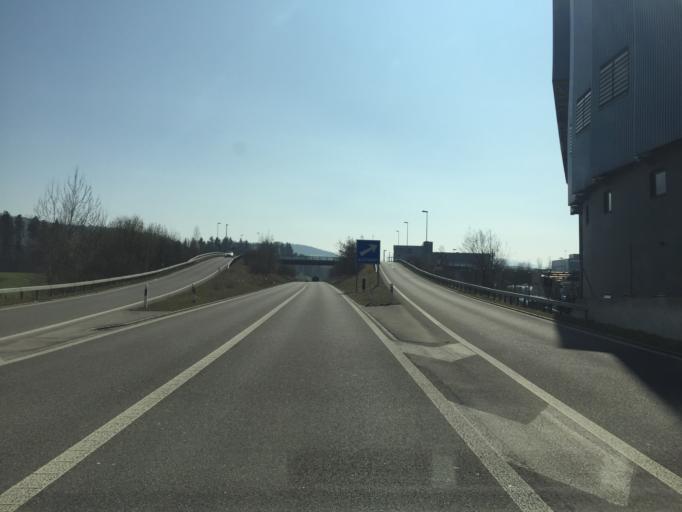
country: CH
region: Saint Gallen
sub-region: Wahlkreis Wil
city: Jonschwil
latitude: 47.4241
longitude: 9.0684
